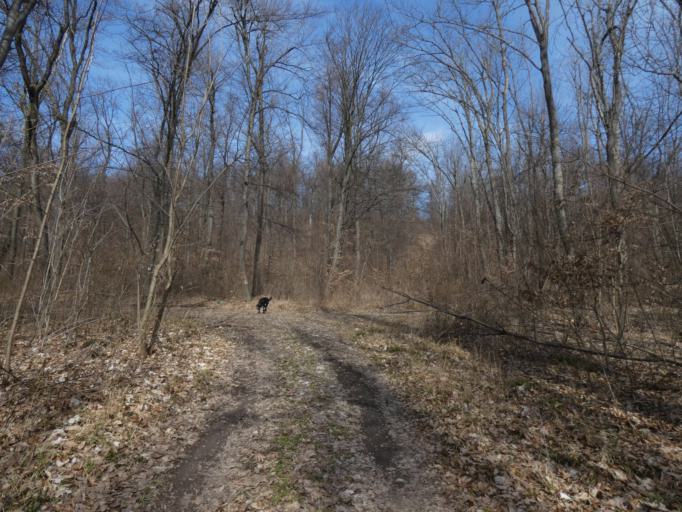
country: HU
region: Pest
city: Telki
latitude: 47.5558
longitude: 18.8728
